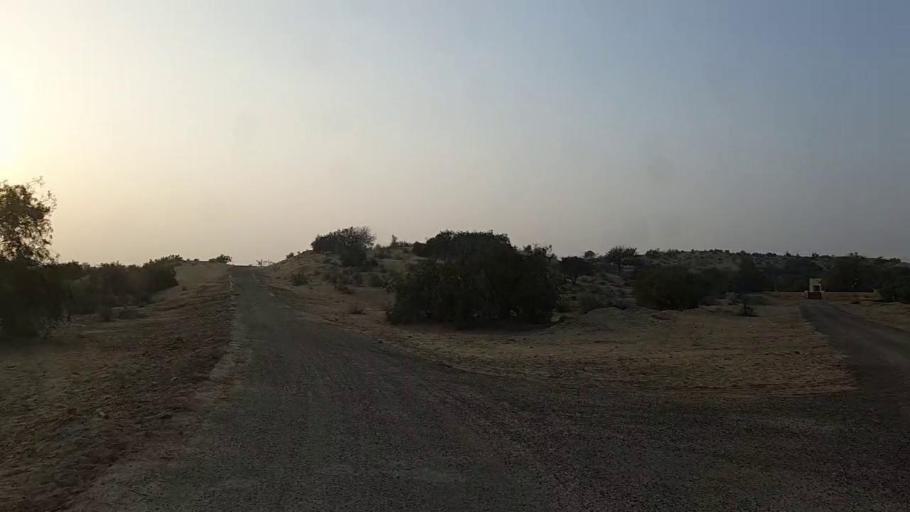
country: PK
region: Sindh
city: Naukot
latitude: 24.6810
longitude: 69.4582
